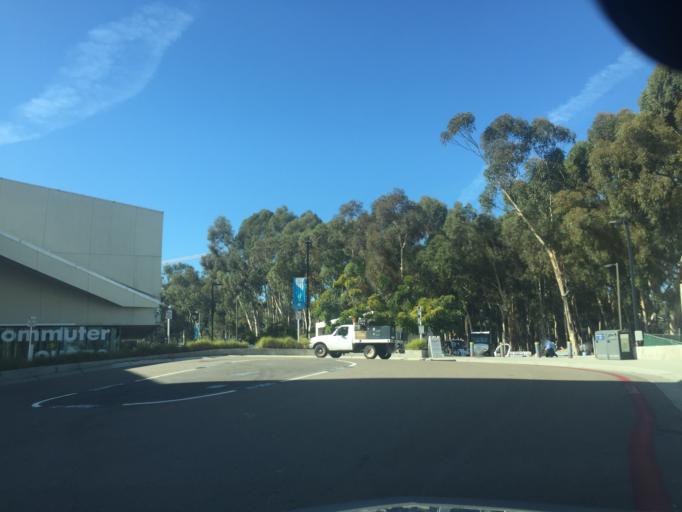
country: US
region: California
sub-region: San Diego County
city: La Jolla
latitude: 32.8802
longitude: -117.2356
